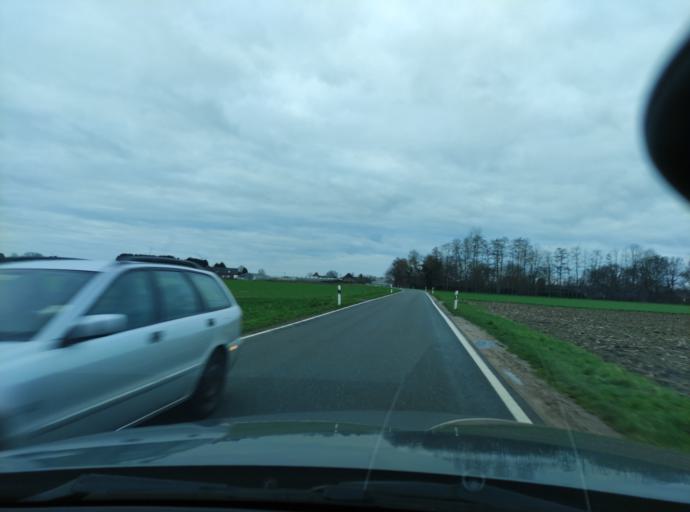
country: DE
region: North Rhine-Westphalia
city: Straelen
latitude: 51.4839
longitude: 6.2623
